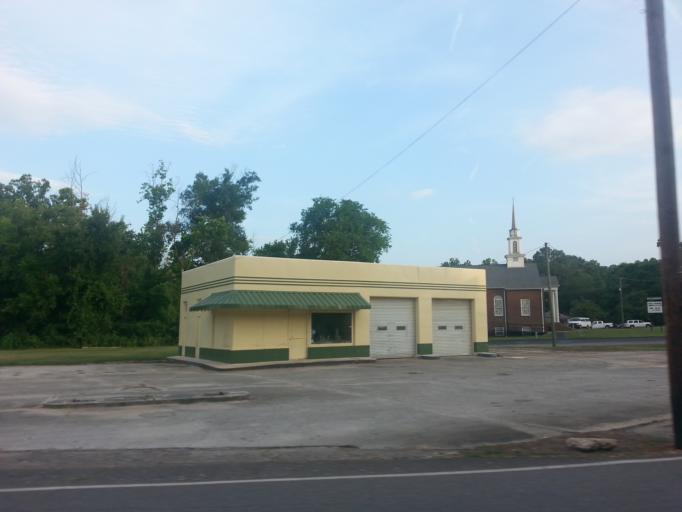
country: US
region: Tennessee
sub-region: Knox County
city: Knoxville
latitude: 35.9842
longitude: -83.8632
